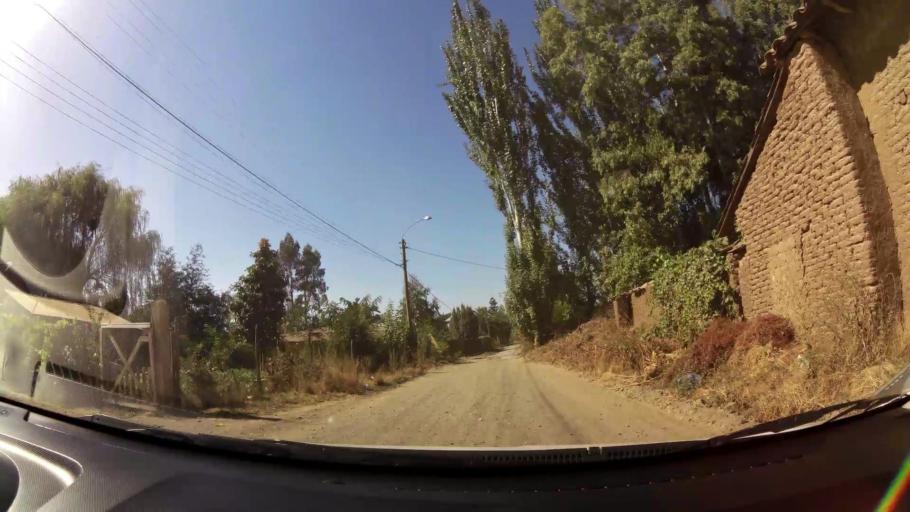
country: CL
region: Maule
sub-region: Provincia de Talca
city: Talca
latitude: -35.4212
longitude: -71.6043
